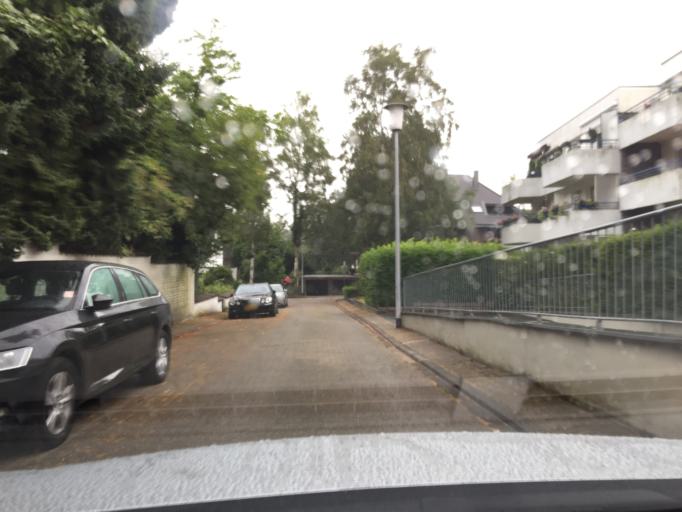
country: DE
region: North Rhine-Westphalia
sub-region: Regierungsbezirk Dusseldorf
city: Ratingen
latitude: 51.3374
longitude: 6.8984
